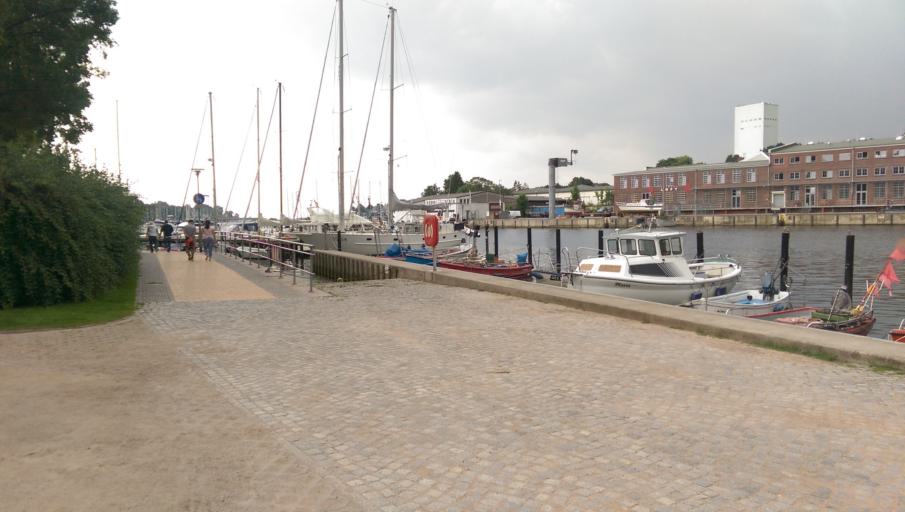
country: DE
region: Schleswig-Holstein
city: Neustadt in Holstein
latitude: 54.1039
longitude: 10.8130
